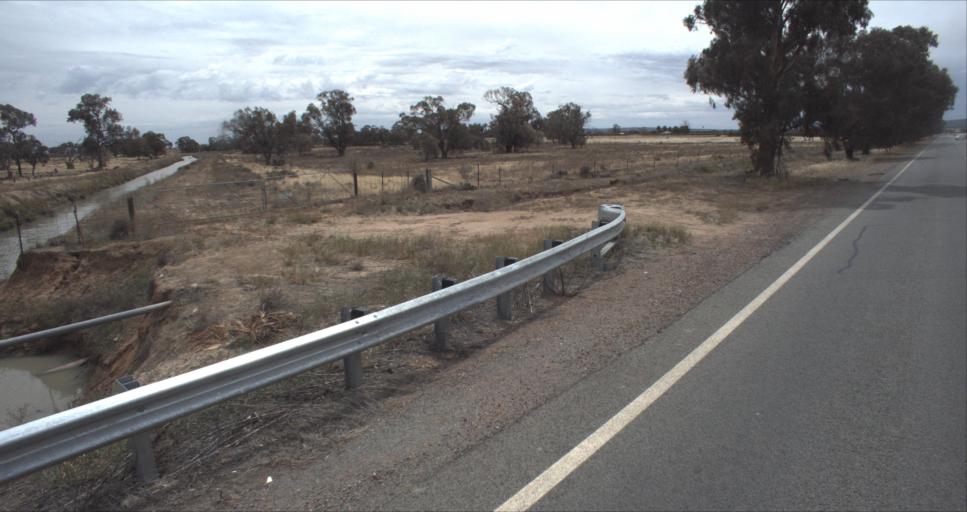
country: AU
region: New South Wales
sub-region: Leeton
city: Leeton
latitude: -34.5150
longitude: 146.4177
